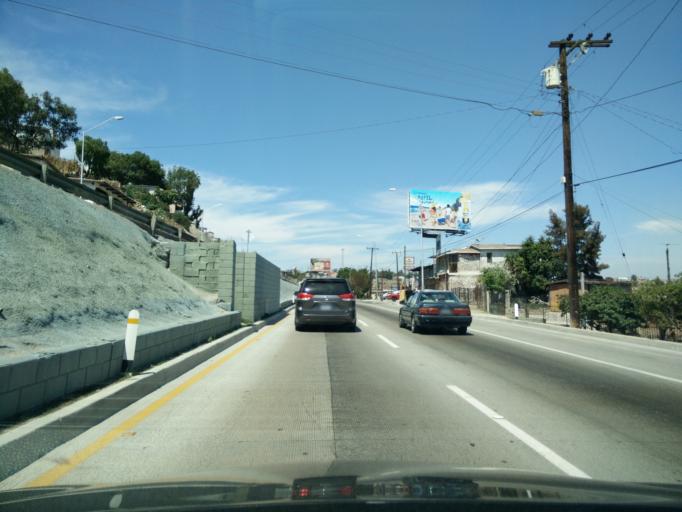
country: MX
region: Baja California
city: Tijuana
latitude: 32.5348
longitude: -116.9970
